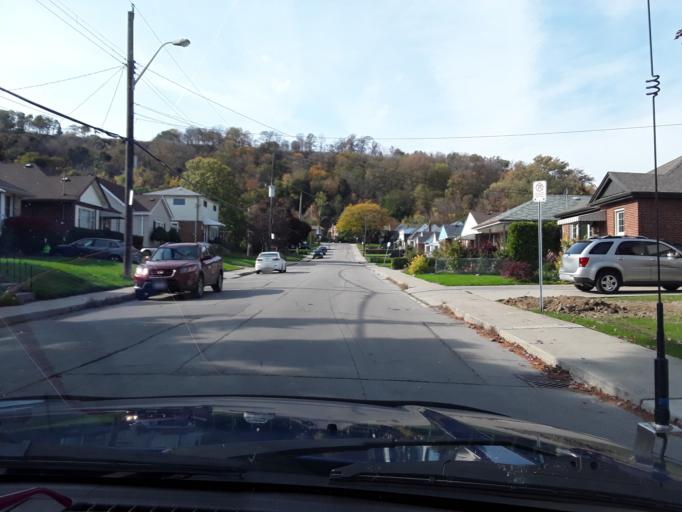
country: CA
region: Ontario
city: Hamilton
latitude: 43.2268
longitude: -79.8110
